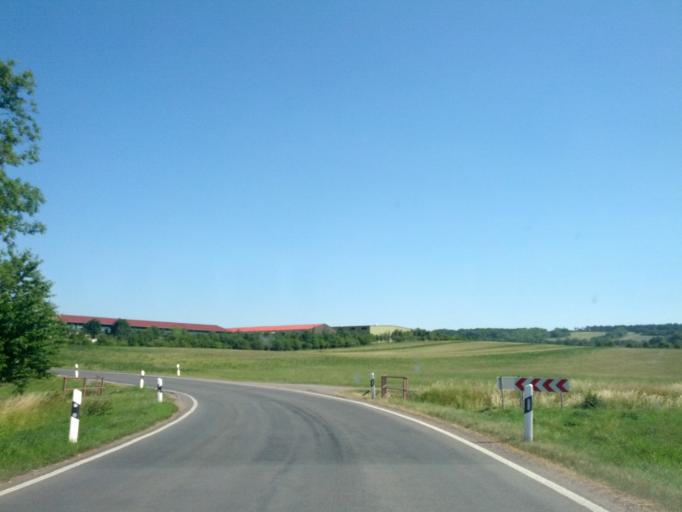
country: DE
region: Thuringia
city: Wandersleben
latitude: 50.8706
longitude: 10.8119
